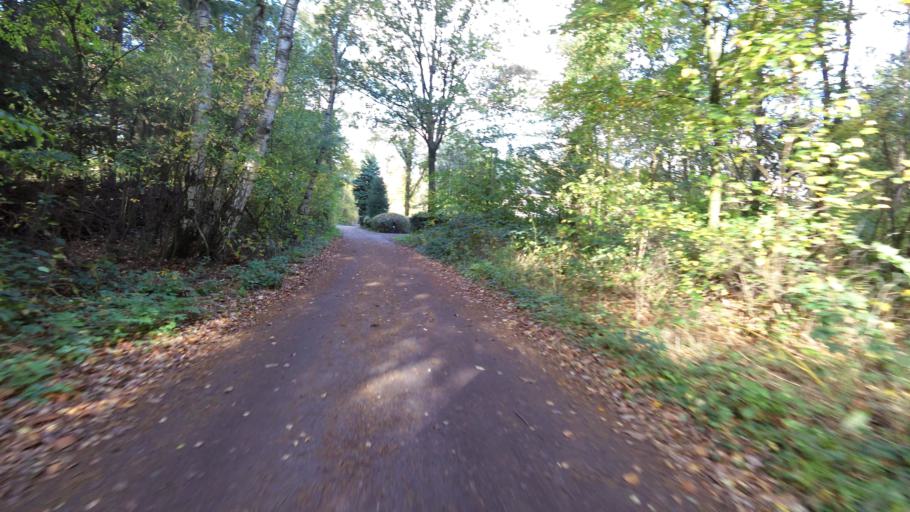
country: NL
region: Gelderland
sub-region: Gemeente Nunspeet
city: Nunspeet
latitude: 52.3386
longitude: 5.8309
